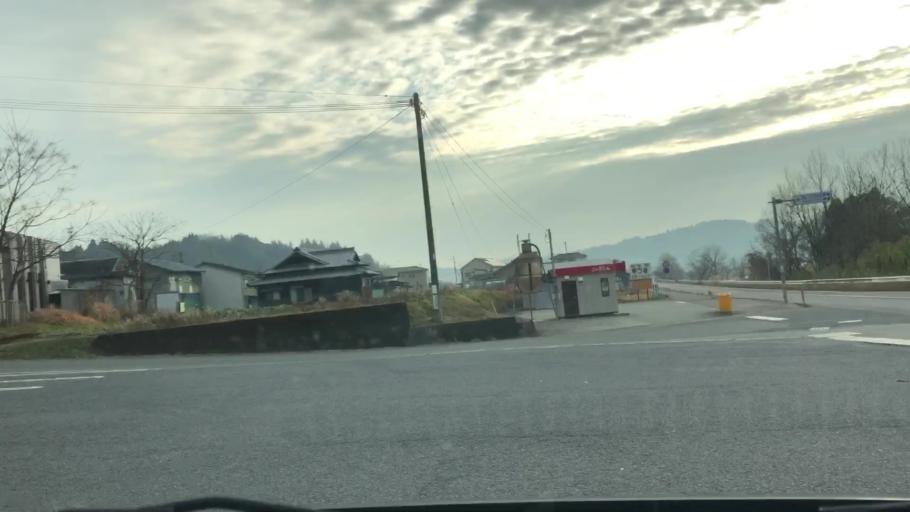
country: JP
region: Oita
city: Takedamachi
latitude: 32.9690
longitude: 131.4748
